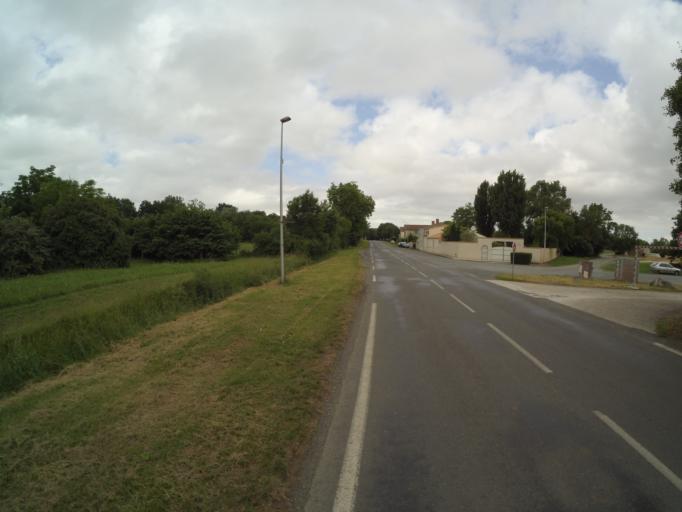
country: FR
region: Poitou-Charentes
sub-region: Departement de la Charente-Maritime
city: Saint-Laurent-de-la-Pree
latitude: 45.9931
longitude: -1.0288
